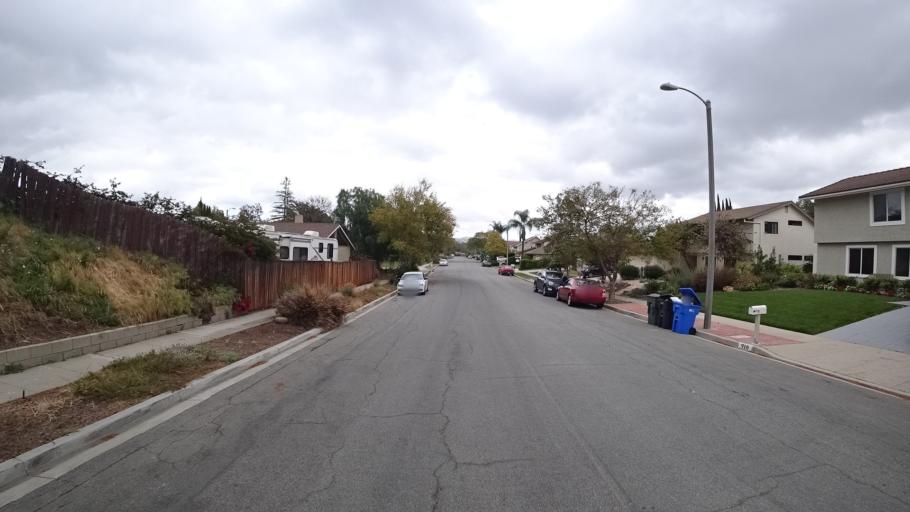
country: US
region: California
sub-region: Ventura County
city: Casa Conejo
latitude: 34.2213
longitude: -118.9019
